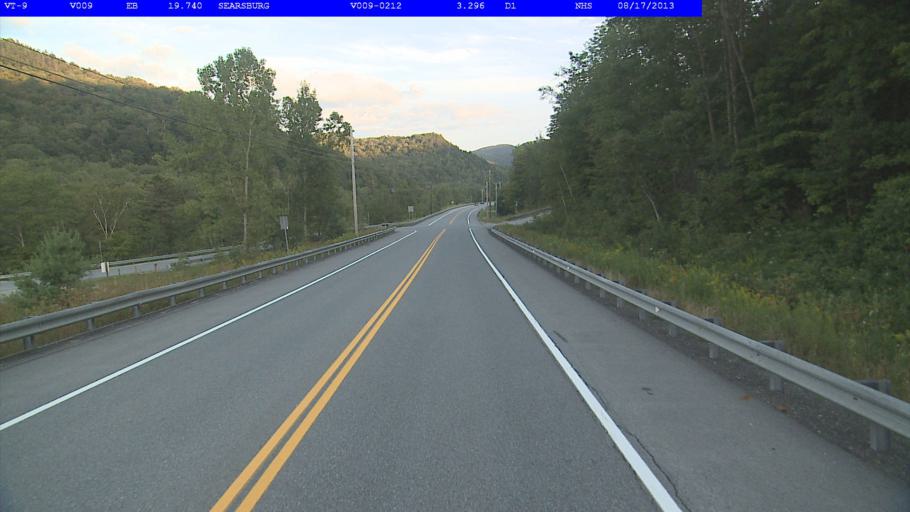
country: US
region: Vermont
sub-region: Windham County
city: Dover
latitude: 42.8903
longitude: -72.9528
